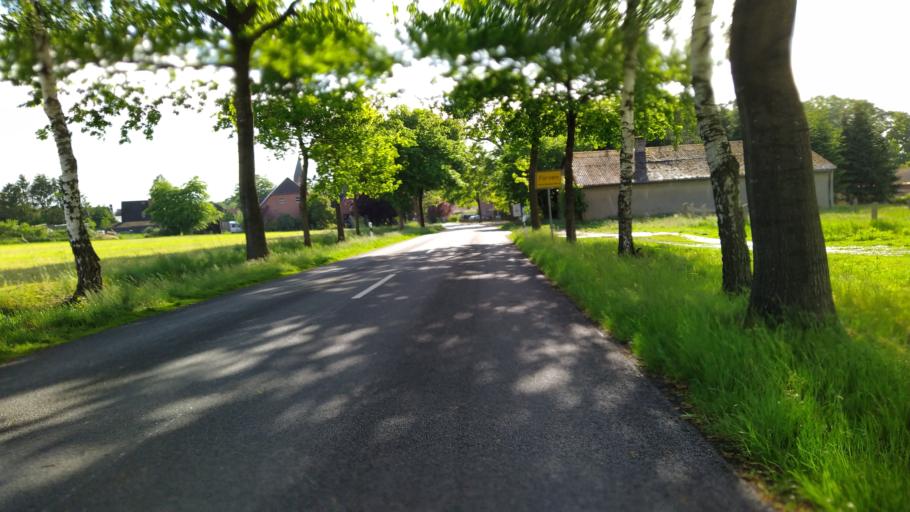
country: DE
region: Lower Saxony
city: Farven
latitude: 53.4368
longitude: 9.3286
